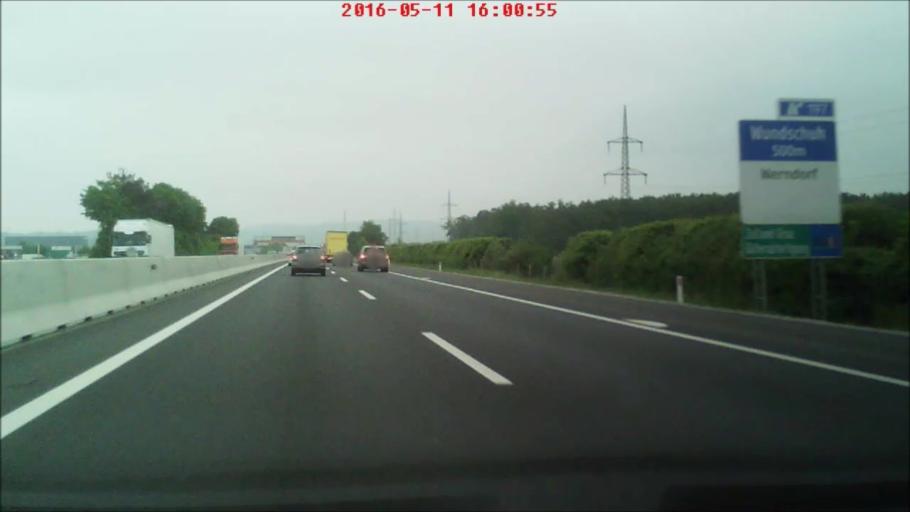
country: AT
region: Styria
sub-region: Politischer Bezirk Graz-Umgebung
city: Wundschuh
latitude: 46.9407
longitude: 15.4569
